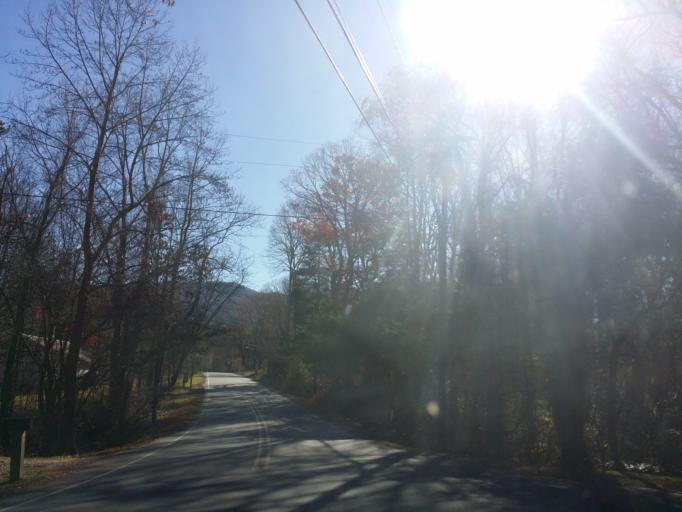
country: US
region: North Carolina
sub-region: Buncombe County
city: Swannanoa
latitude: 35.5975
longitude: -82.4389
